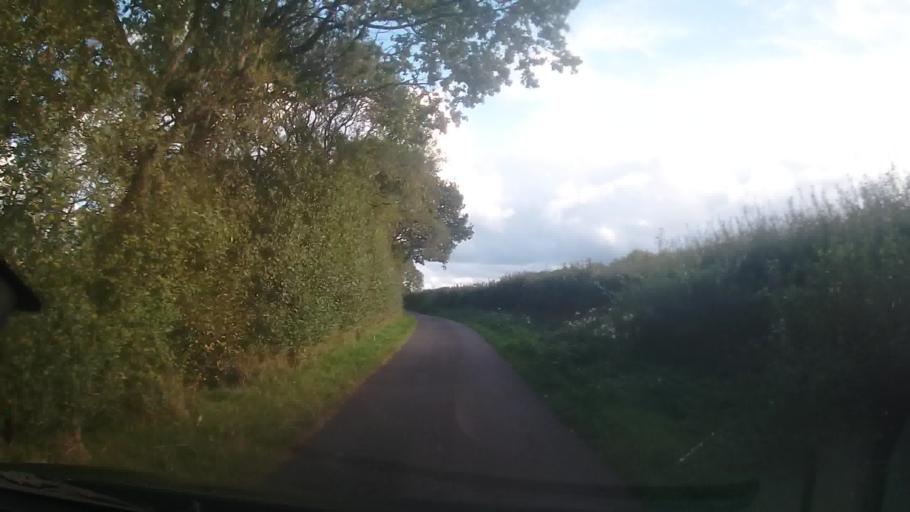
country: GB
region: England
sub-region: Shropshire
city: Wem
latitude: 52.8820
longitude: -2.7335
